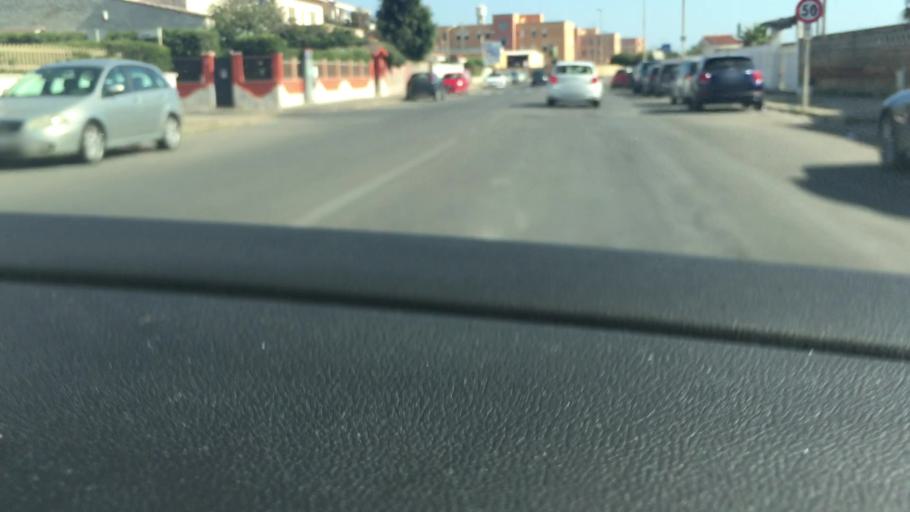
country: IT
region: Latium
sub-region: Citta metropolitana di Roma Capitale
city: Anzio
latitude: 41.4557
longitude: 12.6165
